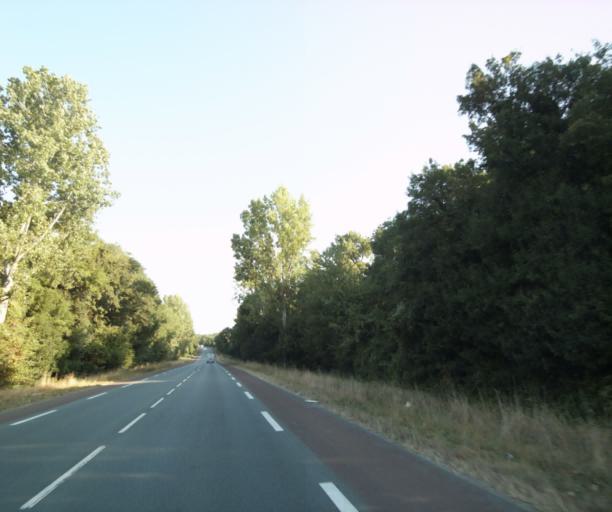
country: FR
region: Poitou-Charentes
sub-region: Departement de la Charente-Maritime
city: Cabariot
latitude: 45.9395
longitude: -0.8640
